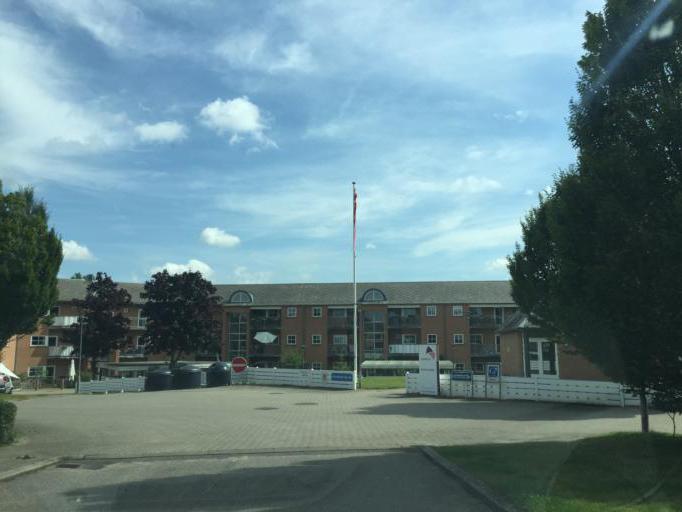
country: DK
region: South Denmark
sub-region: Odense Kommune
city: Hojby
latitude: 55.3340
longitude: 10.4452
